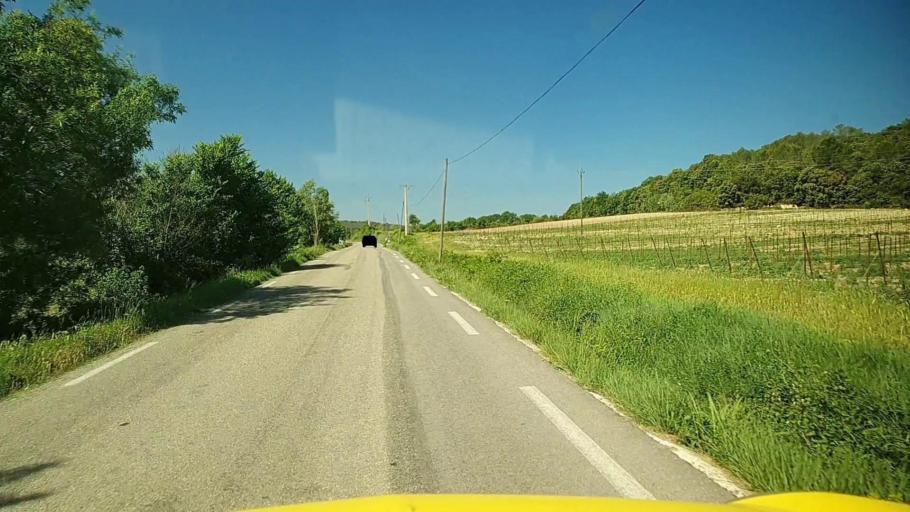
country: FR
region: Languedoc-Roussillon
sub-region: Departement du Gard
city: Blauzac
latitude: 43.9479
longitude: 4.3763
